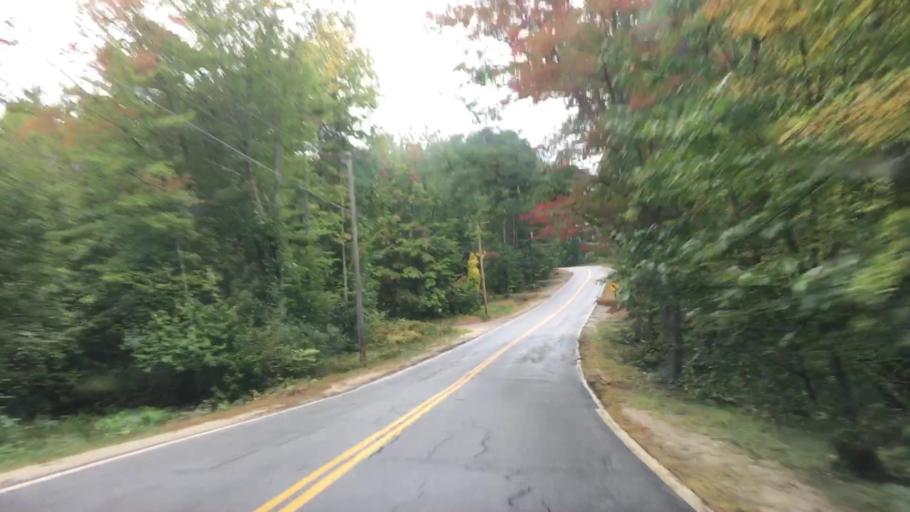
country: US
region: Maine
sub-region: Cumberland County
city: Raymond
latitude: 43.9616
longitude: -70.4652
